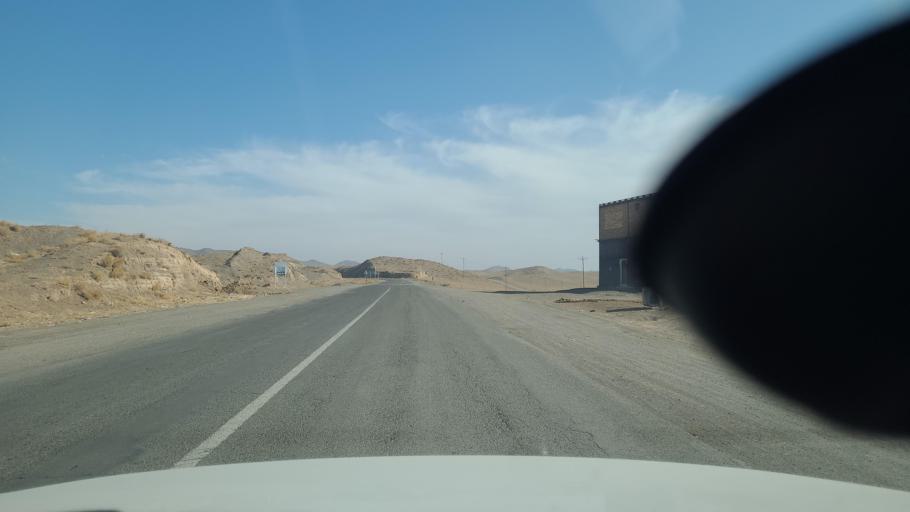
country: IR
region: Razavi Khorasan
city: Fariman
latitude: 35.5924
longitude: 59.6868
